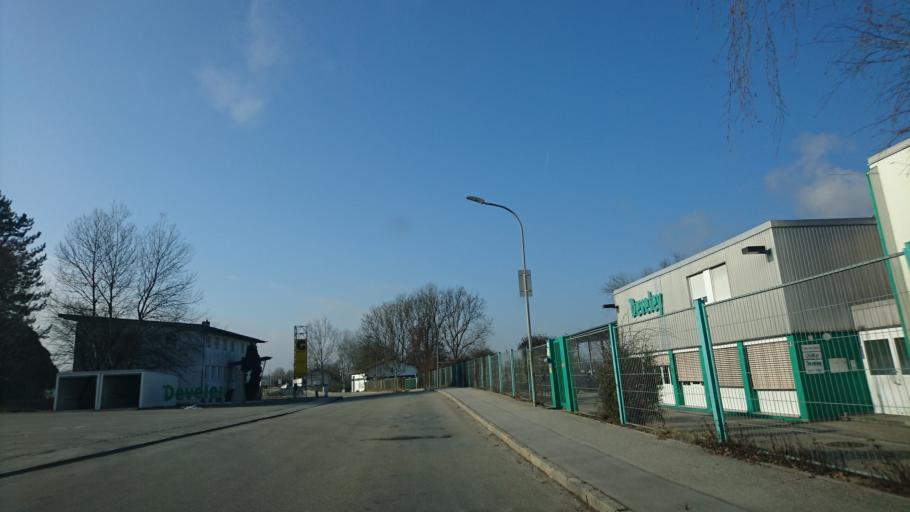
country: DE
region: Bavaria
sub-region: Lower Bavaria
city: Pfarrkirchen
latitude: 48.4217
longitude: 12.9367
